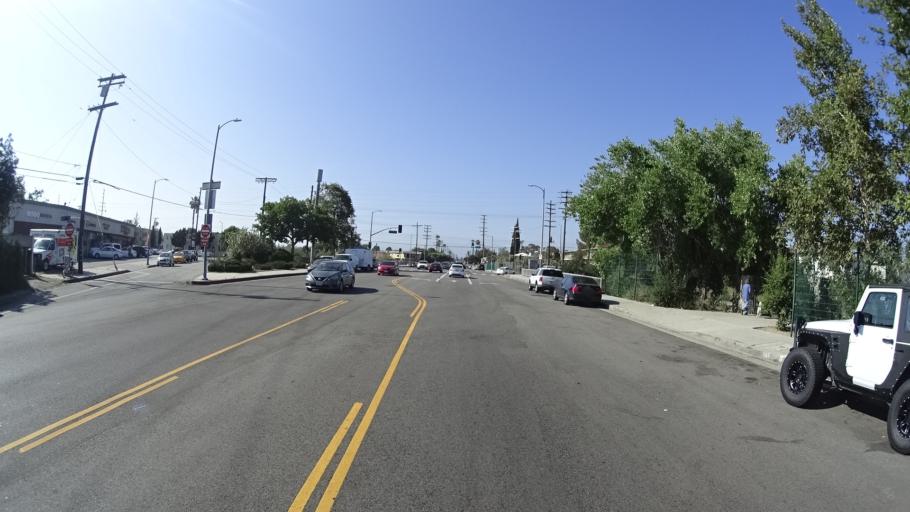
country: US
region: California
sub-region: Los Angeles County
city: Van Nuys
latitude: 34.1931
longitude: -118.4225
